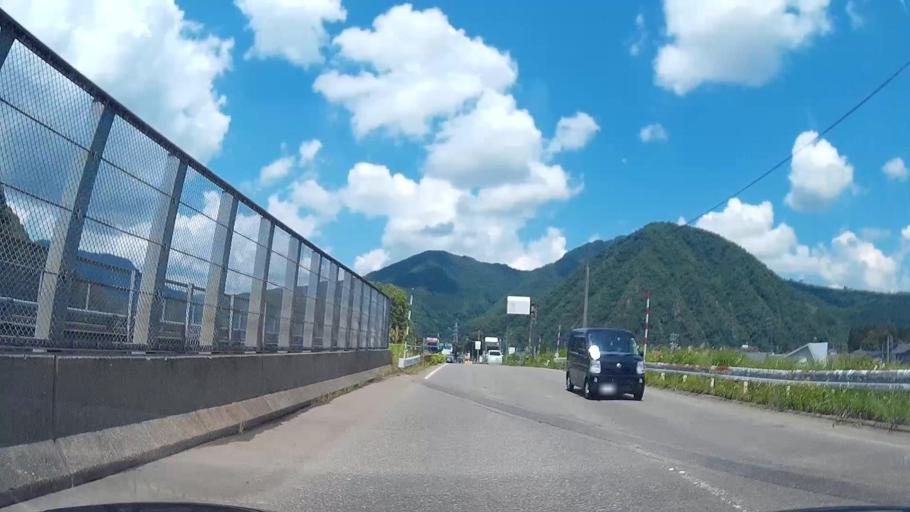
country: JP
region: Niigata
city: Shiozawa
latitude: 36.9278
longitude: 138.8239
